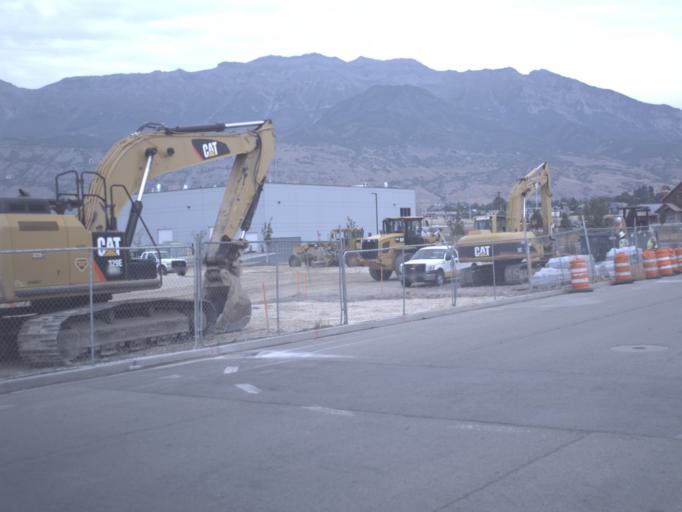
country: US
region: Utah
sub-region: Utah County
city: Lindon
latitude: 40.3263
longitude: -111.7399
